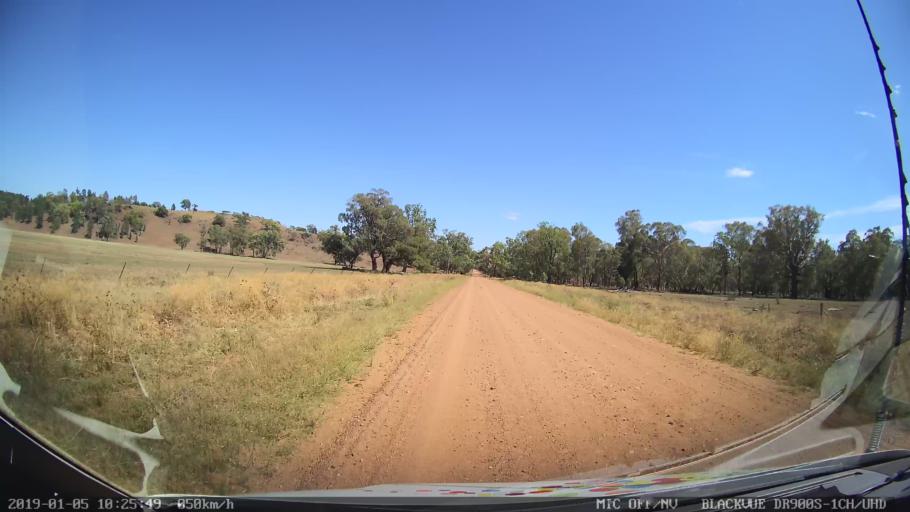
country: AU
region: New South Wales
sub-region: Gilgandra
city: Gilgandra
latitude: -31.5582
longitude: 148.9575
